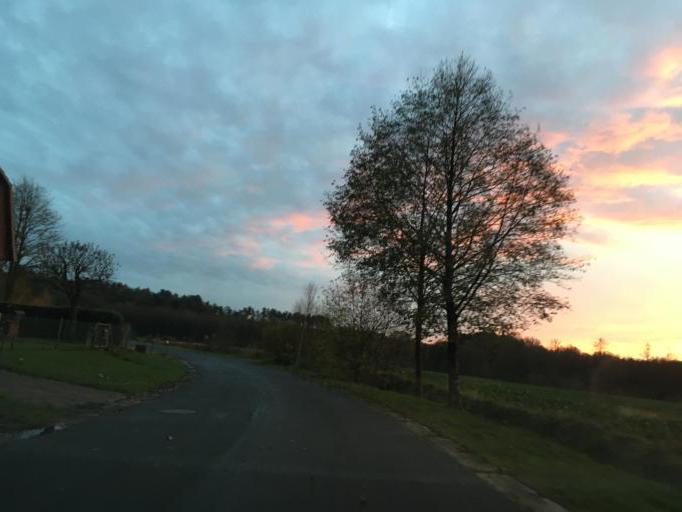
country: DE
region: Lower Saxony
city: Soderstorf
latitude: 53.1200
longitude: 10.1151
